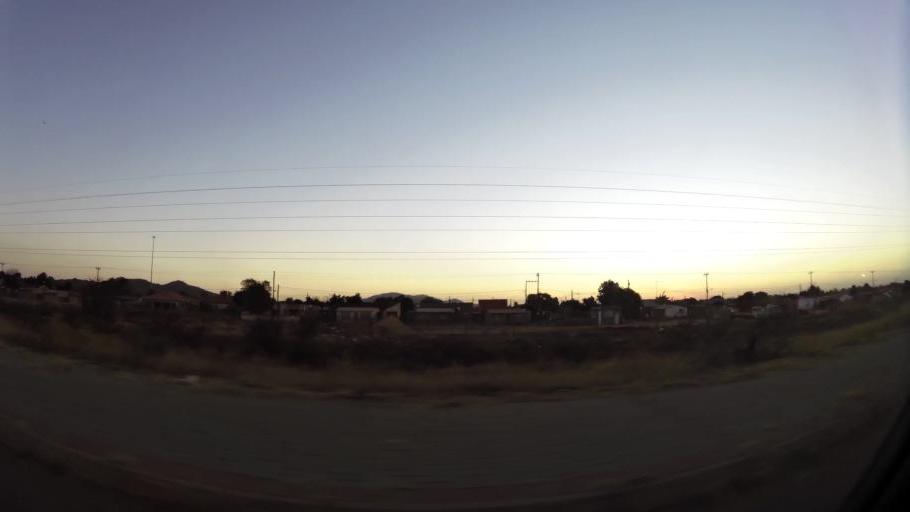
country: ZA
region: North-West
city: Ga-Rankuwa
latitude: -25.5959
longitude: 27.9896
